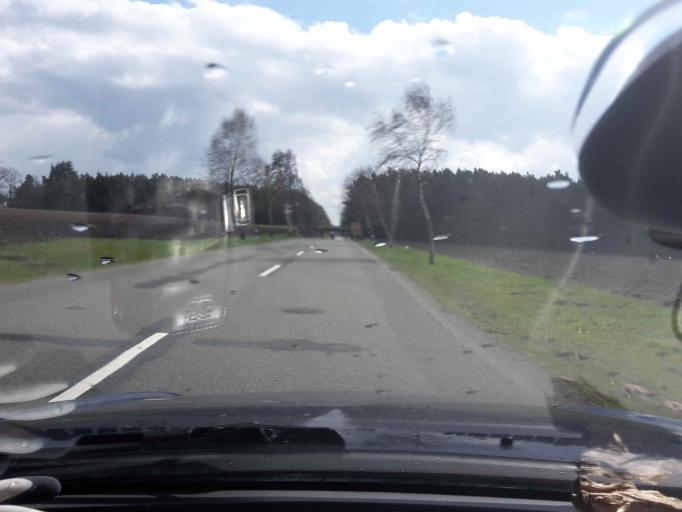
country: DE
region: Lower Saxony
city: Bispingen
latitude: 53.0736
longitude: 9.9686
